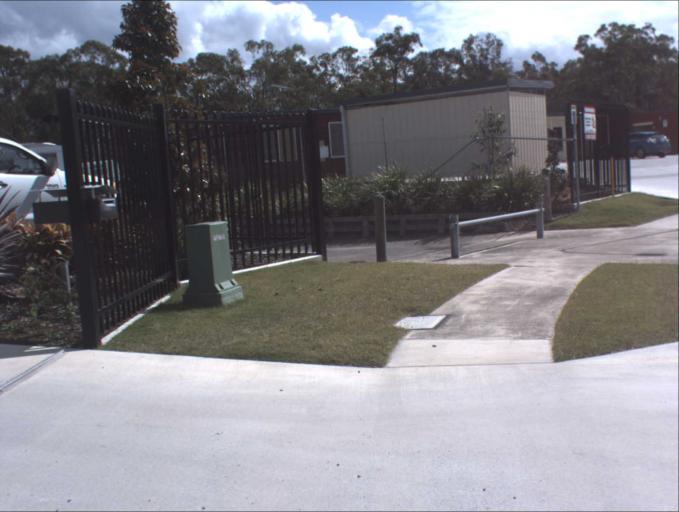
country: AU
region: Queensland
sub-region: Logan
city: Woodridge
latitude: -27.6745
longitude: 153.0748
